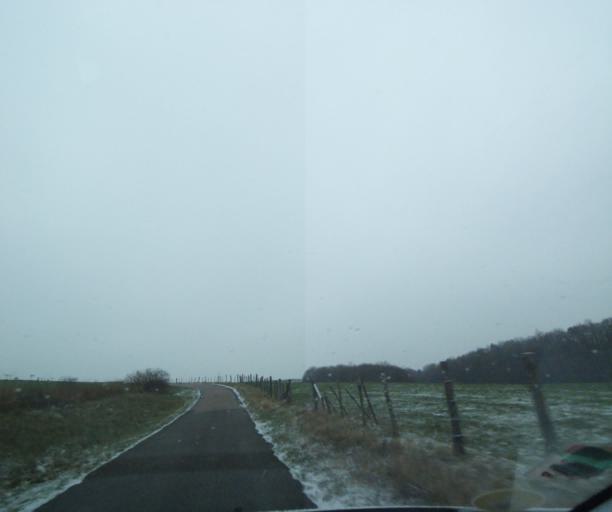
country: FR
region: Champagne-Ardenne
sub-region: Departement de la Haute-Marne
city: Wassy
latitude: 48.4659
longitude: 5.0075
